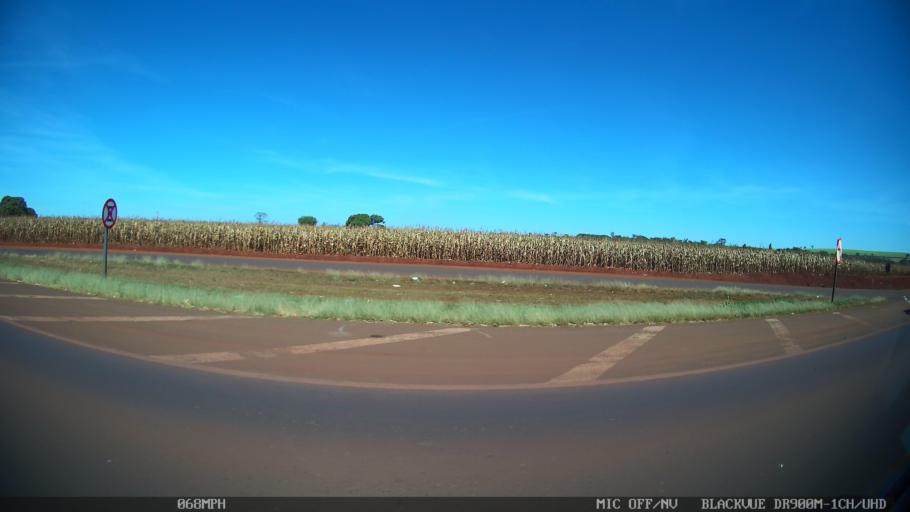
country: BR
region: Sao Paulo
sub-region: Ipua
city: Ipua
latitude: -20.4921
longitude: -47.9961
